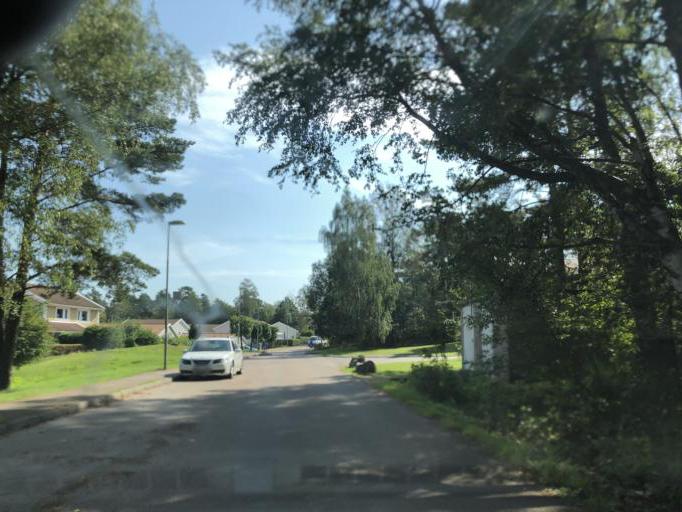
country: SE
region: Vaestra Goetaland
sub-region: Goteborg
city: Goeteborg
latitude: 57.7617
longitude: 11.9638
